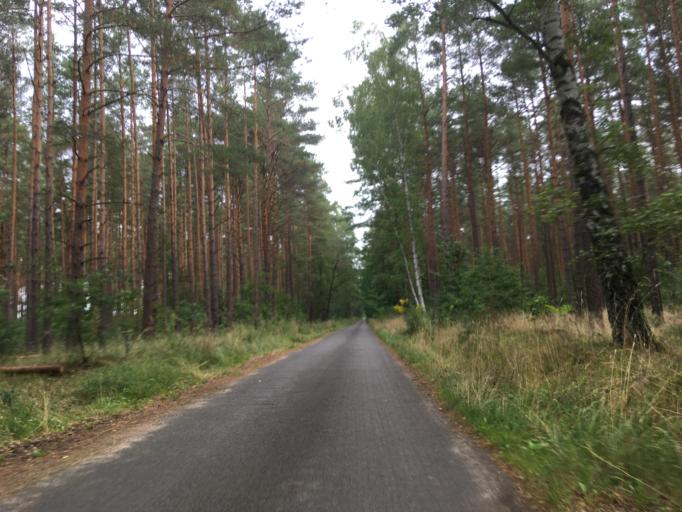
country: DE
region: Brandenburg
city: Rheinsberg
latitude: 53.0760
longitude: 12.9894
